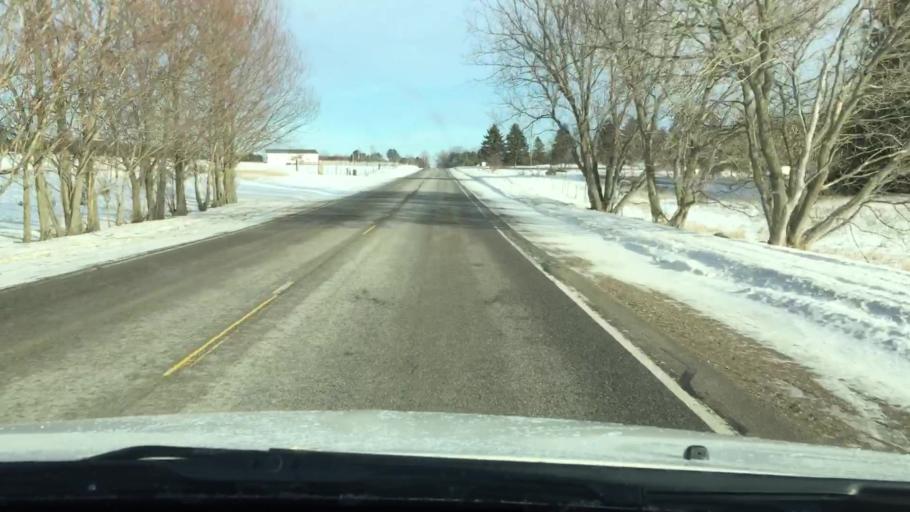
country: US
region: Michigan
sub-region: Kalkaska County
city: Kalkaska
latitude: 44.6404
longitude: -85.2012
